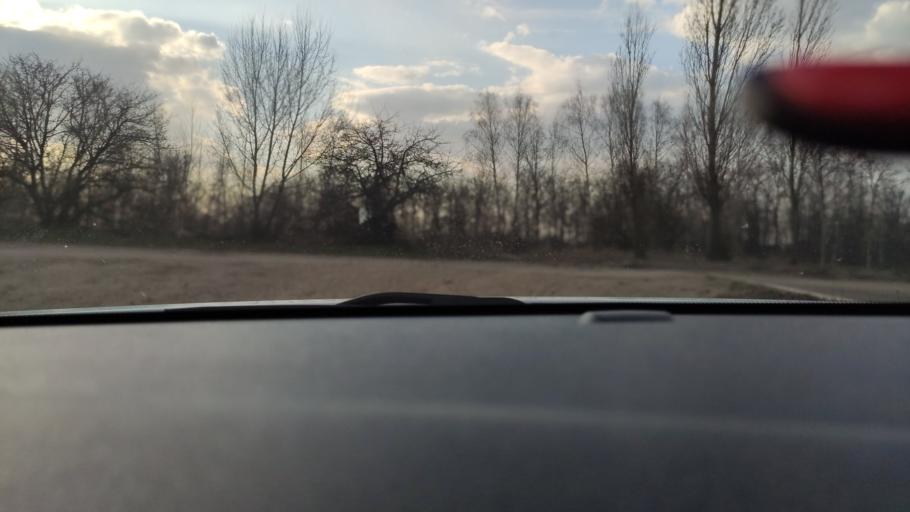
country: RU
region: Voronezj
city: Pridonskoy
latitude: 51.6385
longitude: 39.0916
